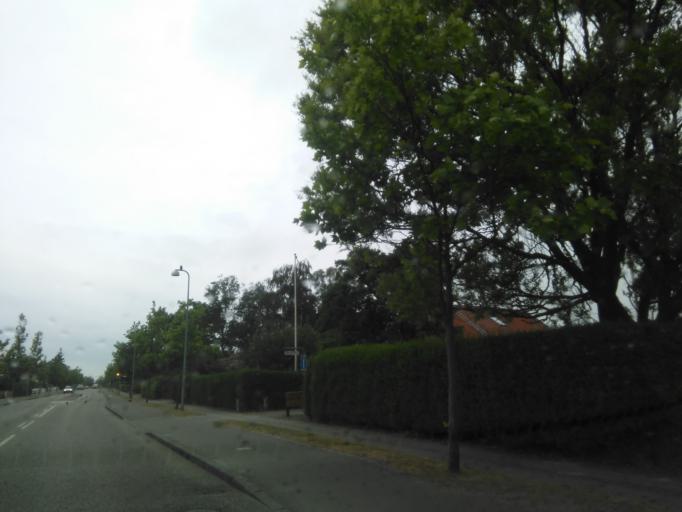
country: DK
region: Capital Region
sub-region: Bornholm Kommune
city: Ronne
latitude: 55.0936
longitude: 14.7254
